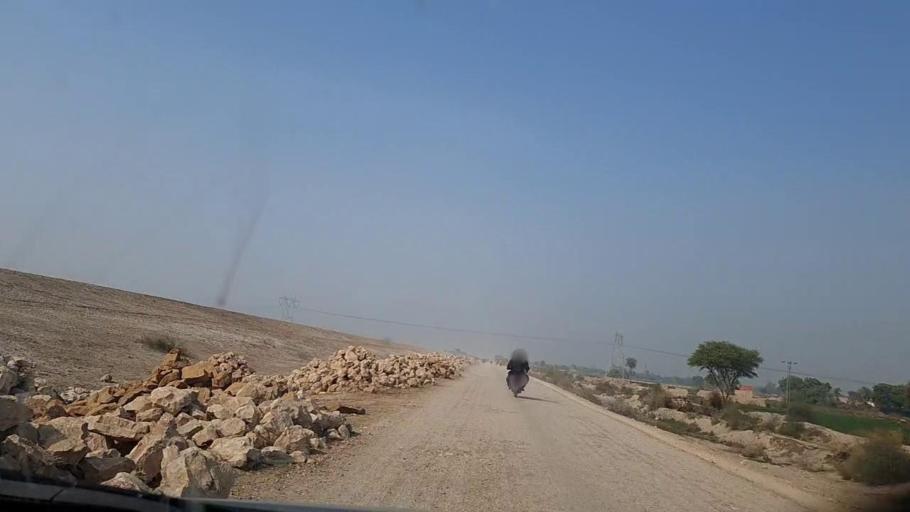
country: PK
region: Sindh
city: Moro
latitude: 26.7077
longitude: 67.9256
